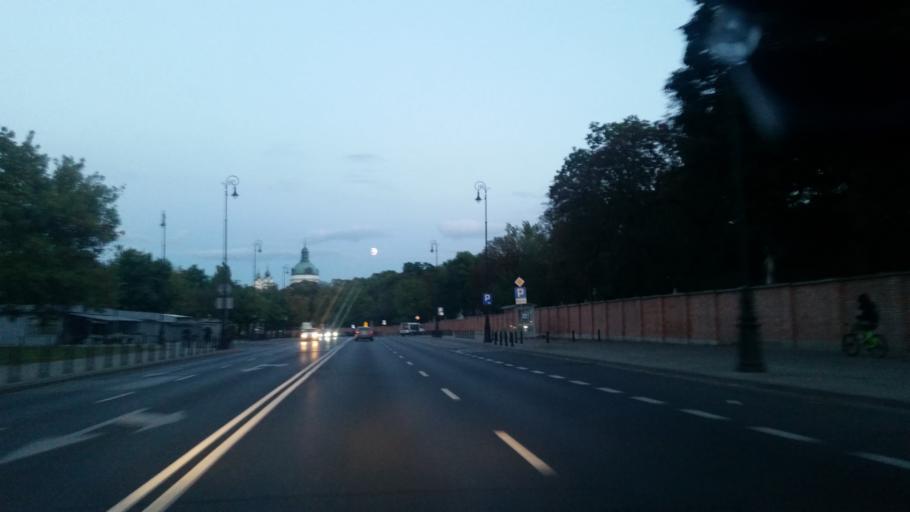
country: PL
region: Masovian Voivodeship
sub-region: Warszawa
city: Zoliborz
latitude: 52.2545
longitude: 20.9733
